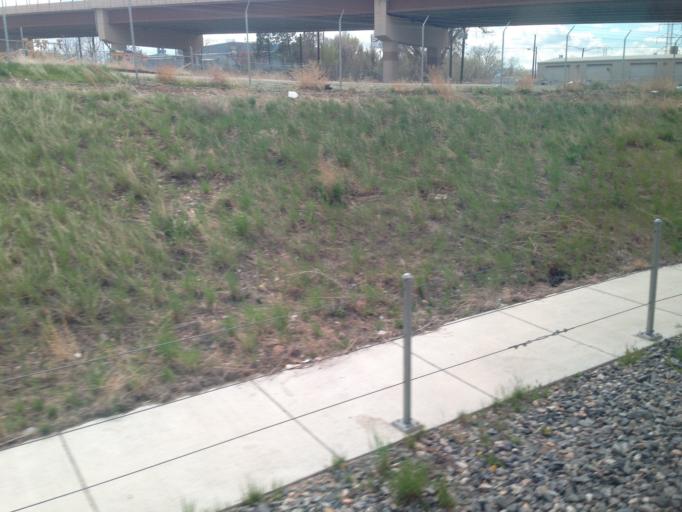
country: US
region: Colorado
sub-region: Adams County
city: Twin Lakes
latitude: 39.8052
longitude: -105.0056
